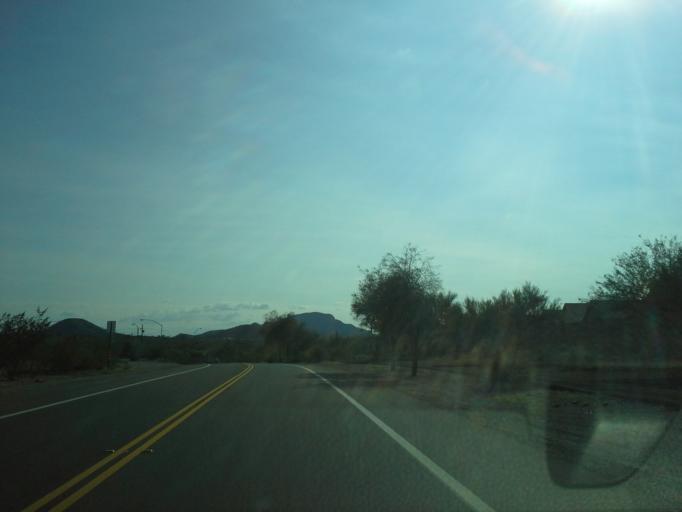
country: US
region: Arizona
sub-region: Pima County
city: Flowing Wells
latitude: 32.2379
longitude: -111.0210
